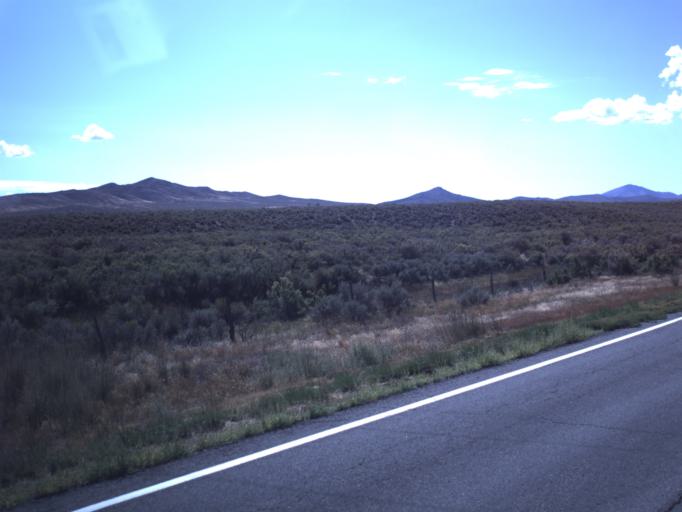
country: US
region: Utah
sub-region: Tooele County
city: Tooele
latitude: 40.1615
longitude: -112.4308
